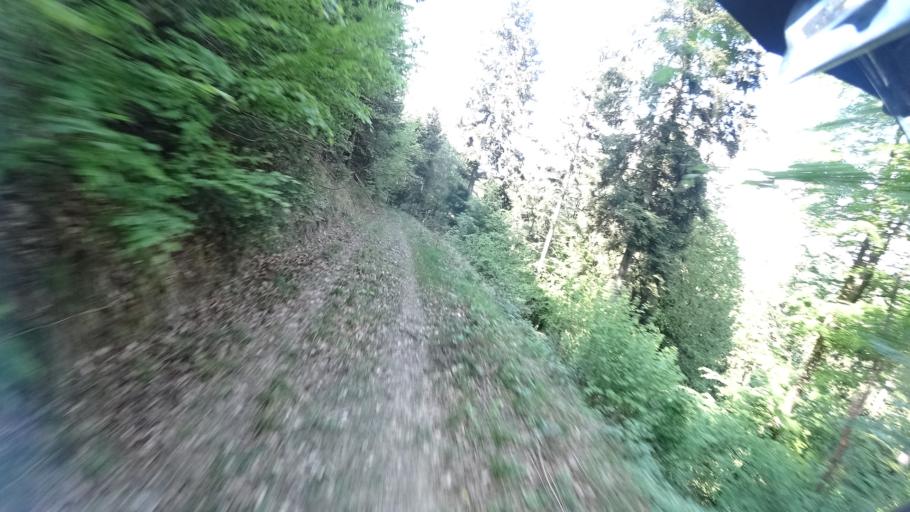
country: HR
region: Grad Zagreb
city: Kasina
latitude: 45.9449
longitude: 15.9829
